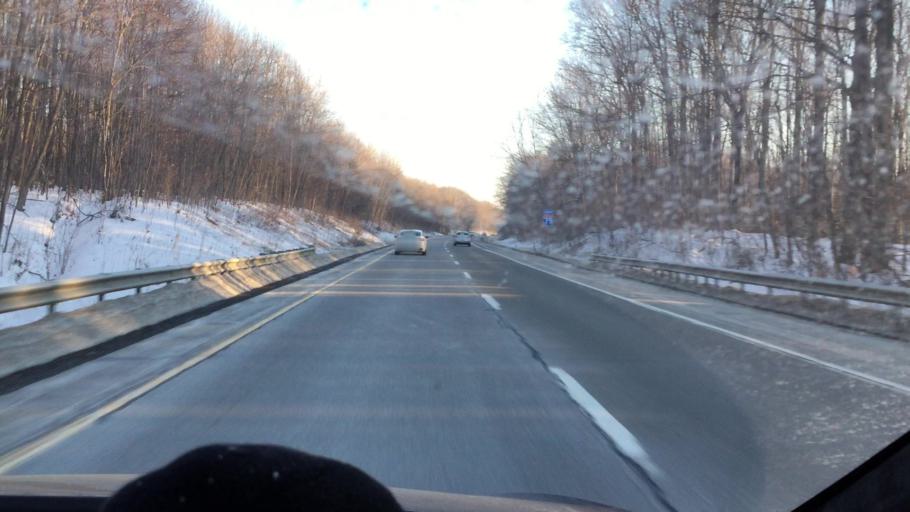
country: US
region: Pennsylvania
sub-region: Crawford County
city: Meadville
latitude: 41.7104
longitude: -80.1995
